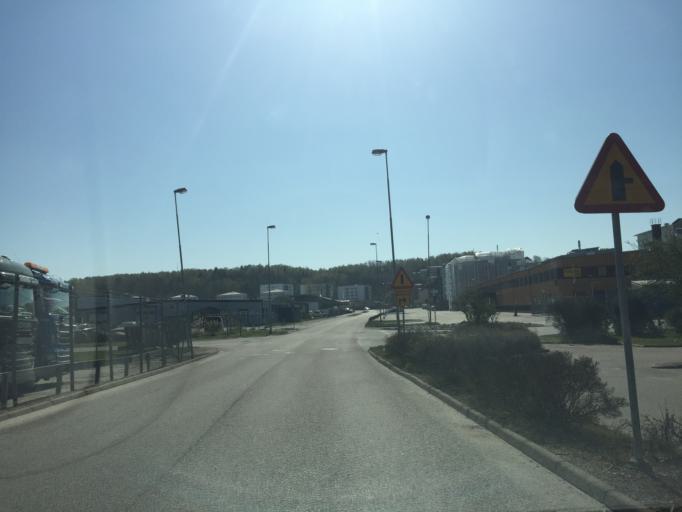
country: SE
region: Vaestra Goetaland
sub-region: Kungalvs Kommun
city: Kungalv
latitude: 57.8782
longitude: 11.9792
